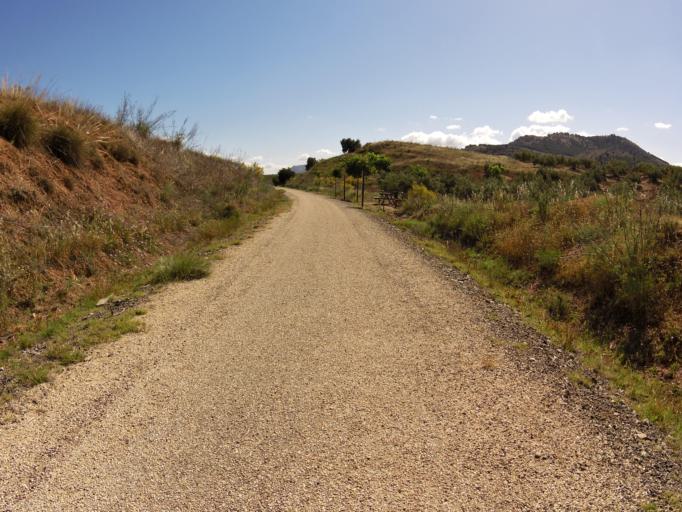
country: ES
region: Andalusia
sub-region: Provincia de Jaen
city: Alcaudete
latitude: 37.6011
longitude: -4.1389
